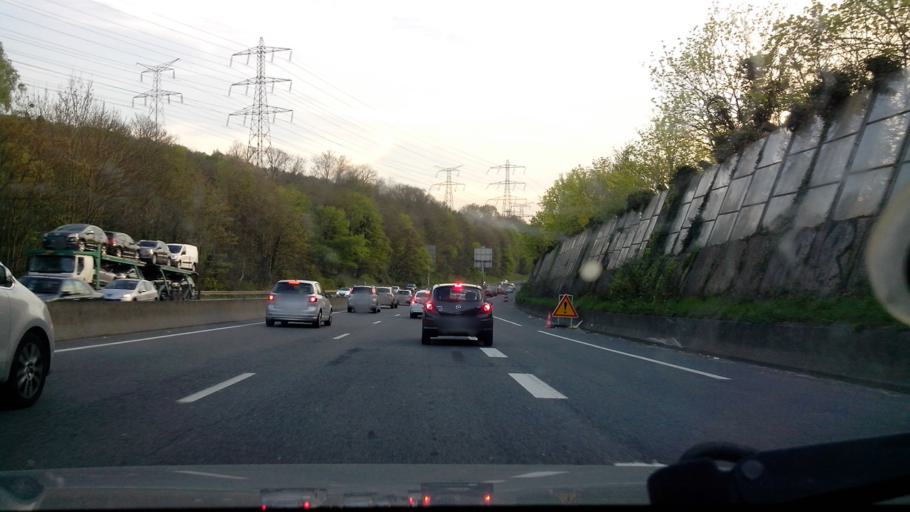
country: FR
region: Ile-de-France
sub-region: Departement de l'Essonne
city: Bievres
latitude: 48.7640
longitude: 2.2293
